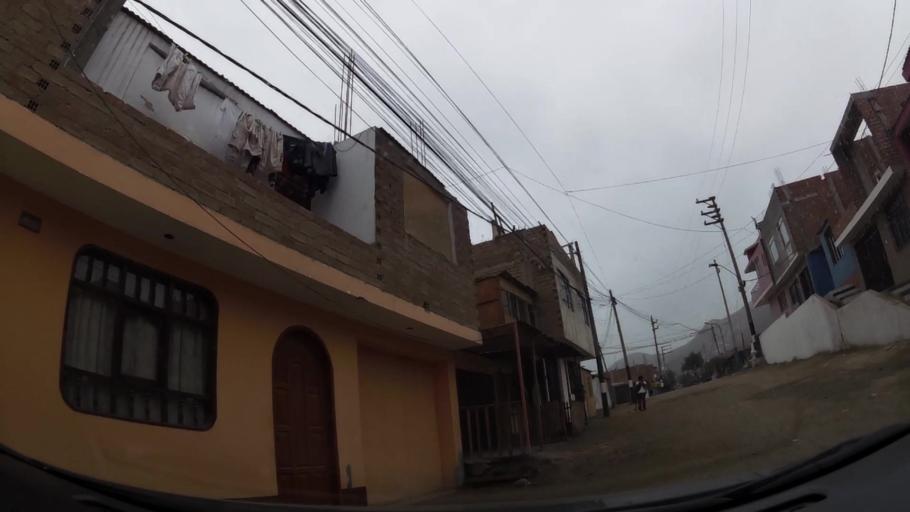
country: PE
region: Lima
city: Ventanilla
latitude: -11.8818
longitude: -77.1334
